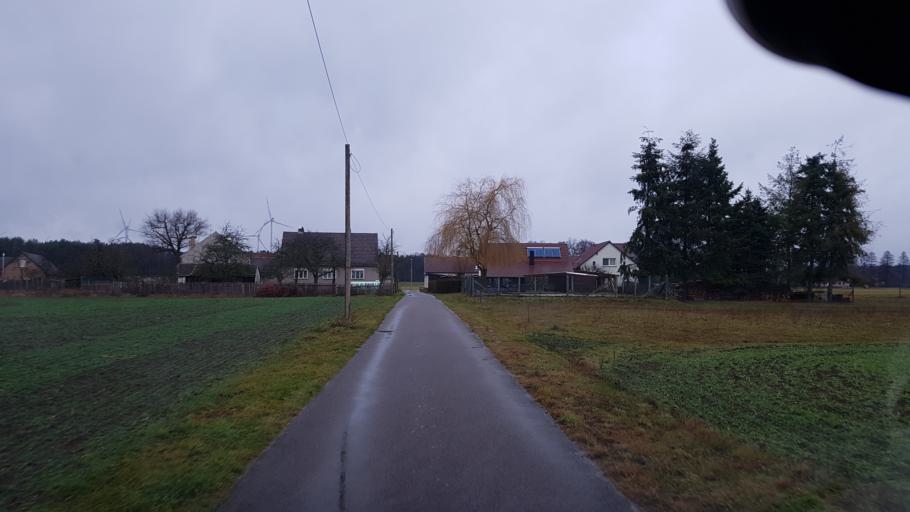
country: DE
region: Brandenburg
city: Sallgast
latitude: 51.6381
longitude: 13.8504
